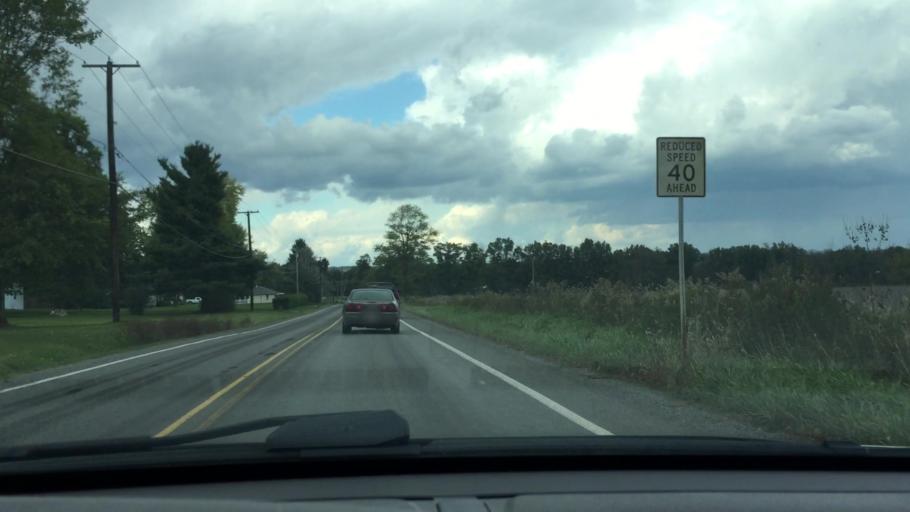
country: US
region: Pennsylvania
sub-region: Lawrence County
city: Oakwood
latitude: 40.9977
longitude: -80.4373
